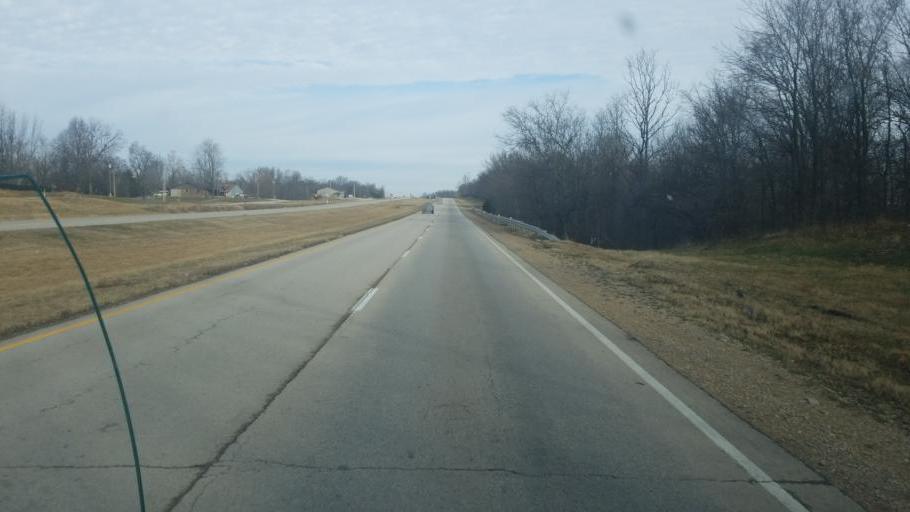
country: US
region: Missouri
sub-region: Stoddard County
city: Dexter
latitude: 36.8266
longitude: -89.9413
